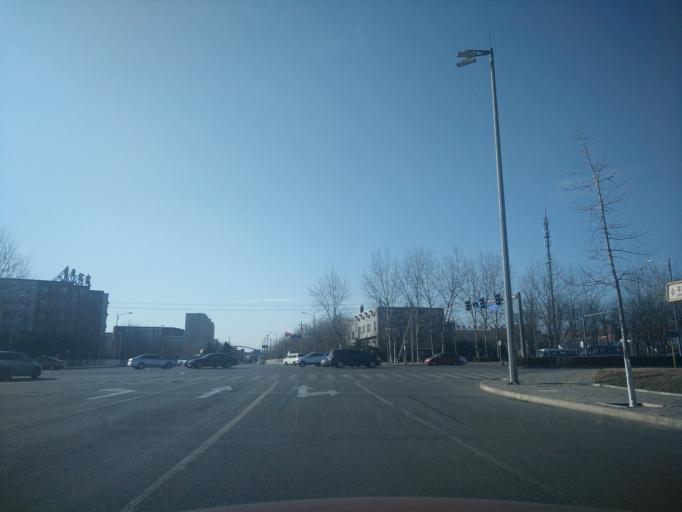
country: CN
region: Beijing
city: Jiugong
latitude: 39.7656
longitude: 116.5089
